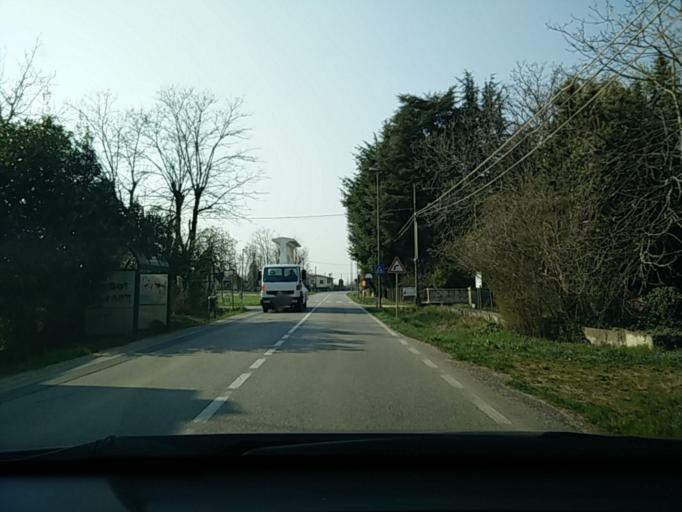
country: IT
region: Veneto
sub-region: Provincia di Treviso
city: Santandra
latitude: 45.7334
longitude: 12.1895
